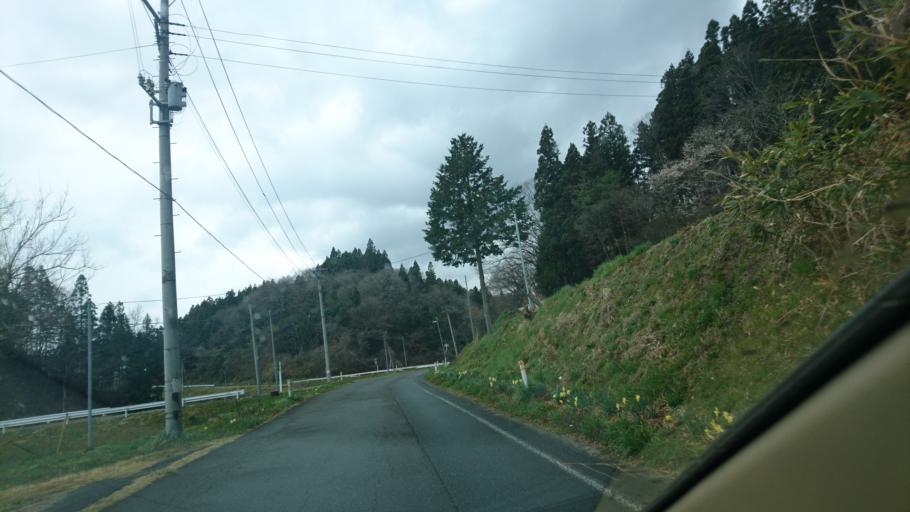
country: JP
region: Iwate
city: Ichinoseki
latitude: 38.9423
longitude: 141.3270
